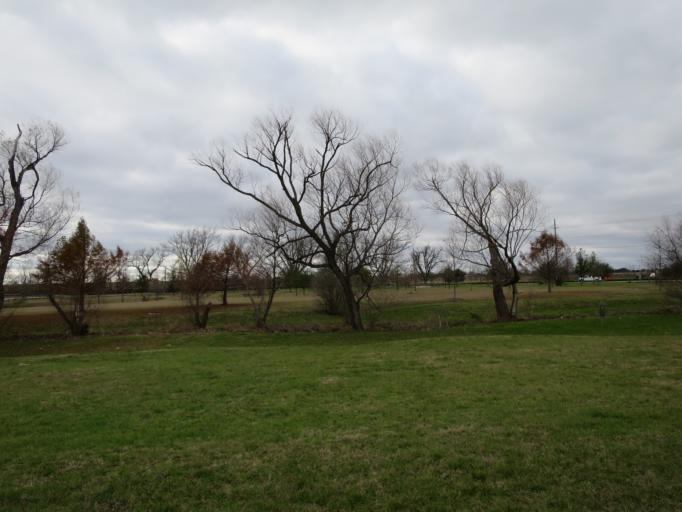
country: US
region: Texas
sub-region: Williamson County
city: Round Rock
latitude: 30.5428
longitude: -97.6279
